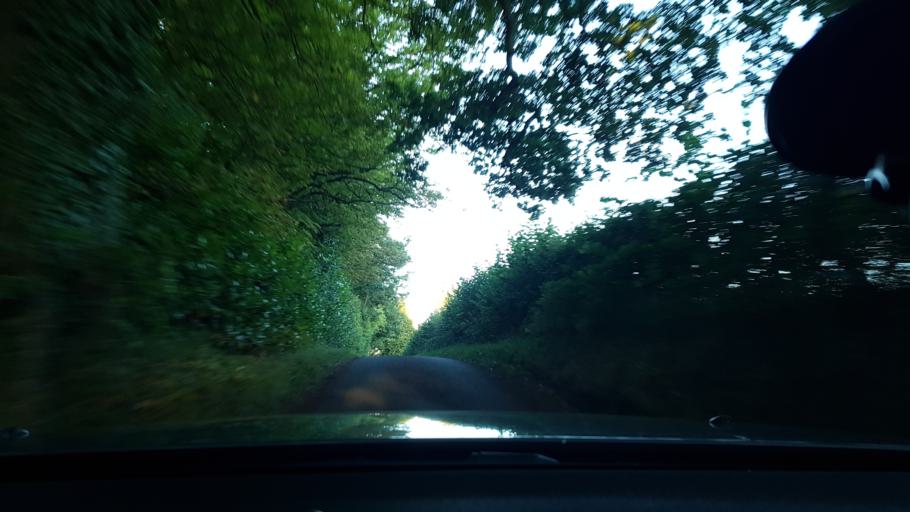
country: GB
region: England
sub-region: Wiltshire
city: Shalbourne
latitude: 51.3869
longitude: -1.5547
